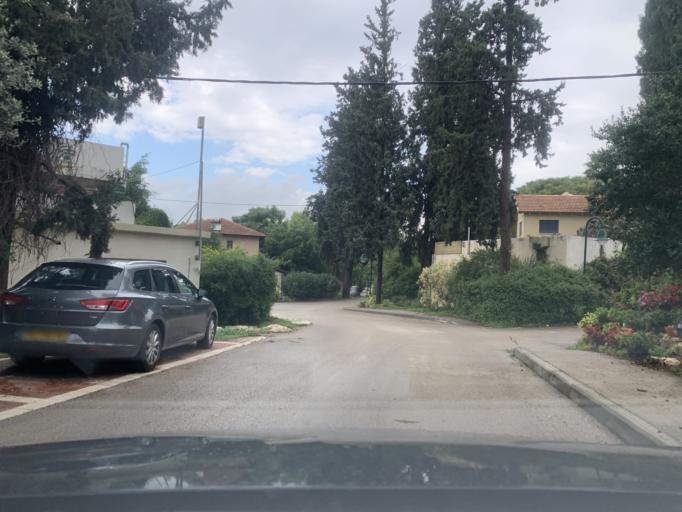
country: PS
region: West Bank
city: Qalqilyah
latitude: 32.2131
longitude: 34.9804
